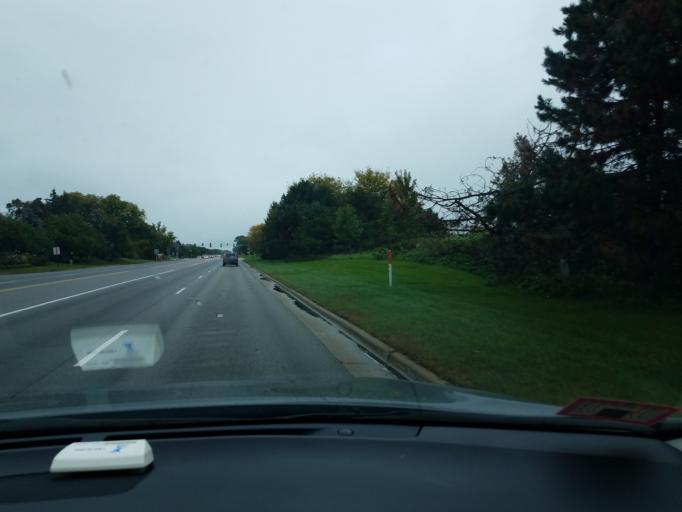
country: US
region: Illinois
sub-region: Lake County
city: Lincolnshire
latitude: 42.1908
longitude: -87.9294
